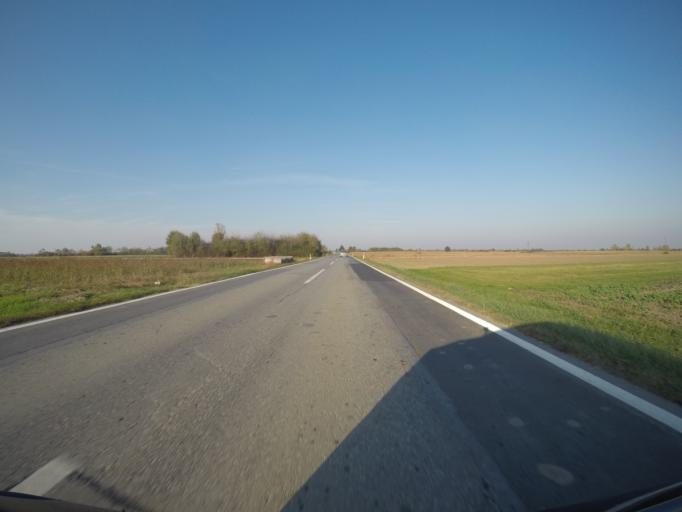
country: HU
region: Somogy
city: Barcs
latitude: 45.9181
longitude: 17.4498
